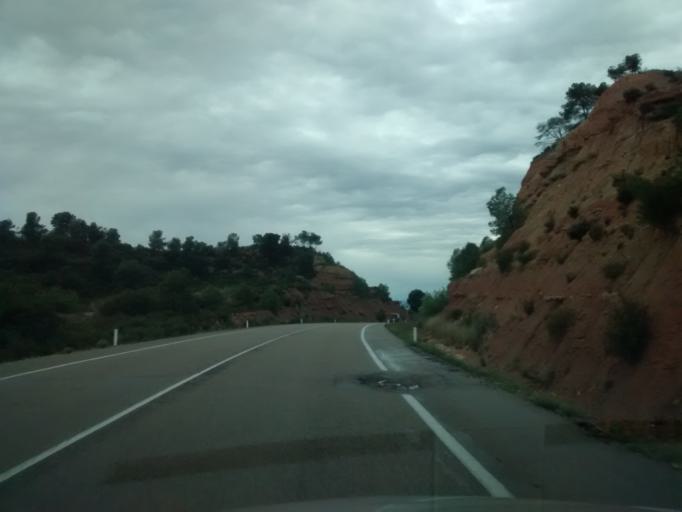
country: ES
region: Aragon
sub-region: Provincia de Zaragoza
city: Maella
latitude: 41.1596
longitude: 0.0841
